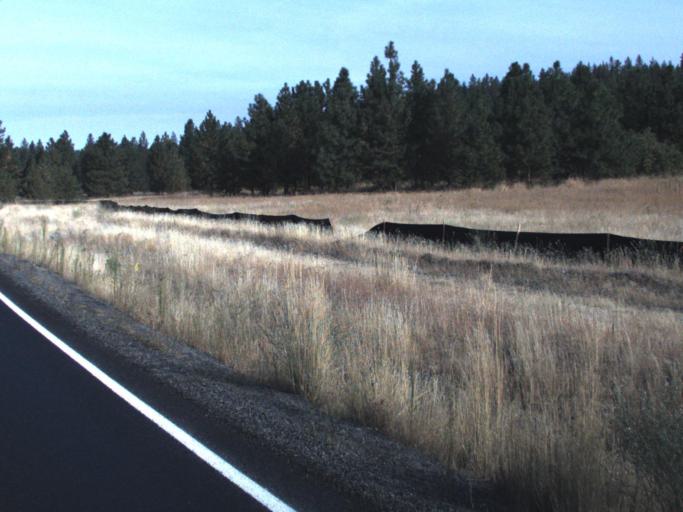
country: US
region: Washington
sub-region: Spokane County
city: Deer Park
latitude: 47.8255
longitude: -117.5936
